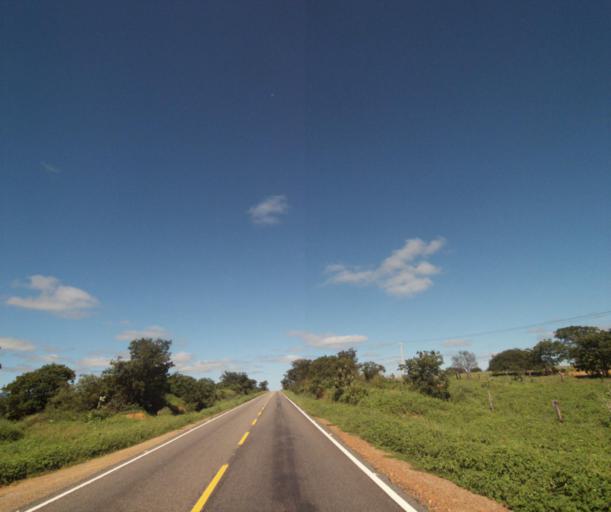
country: BR
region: Bahia
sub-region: Guanambi
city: Guanambi
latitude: -14.2340
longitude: -42.9697
